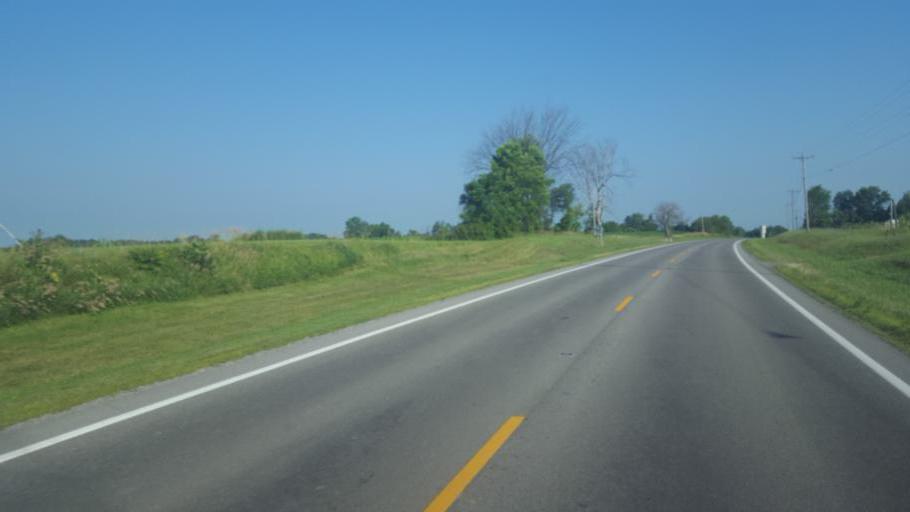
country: US
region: Ohio
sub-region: Hardin County
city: Kenton
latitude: 40.5516
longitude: -83.5351
